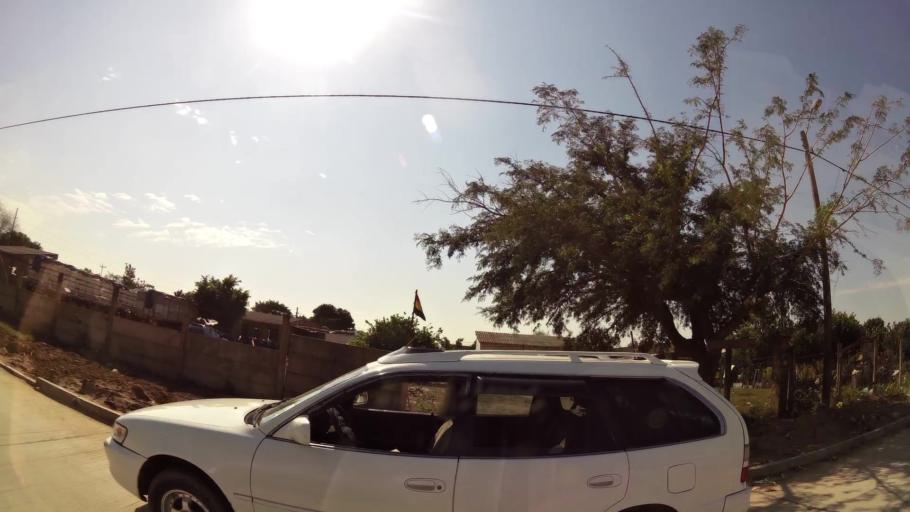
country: BO
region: Santa Cruz
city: Cotoca
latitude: -17.7513
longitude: -63.0933
